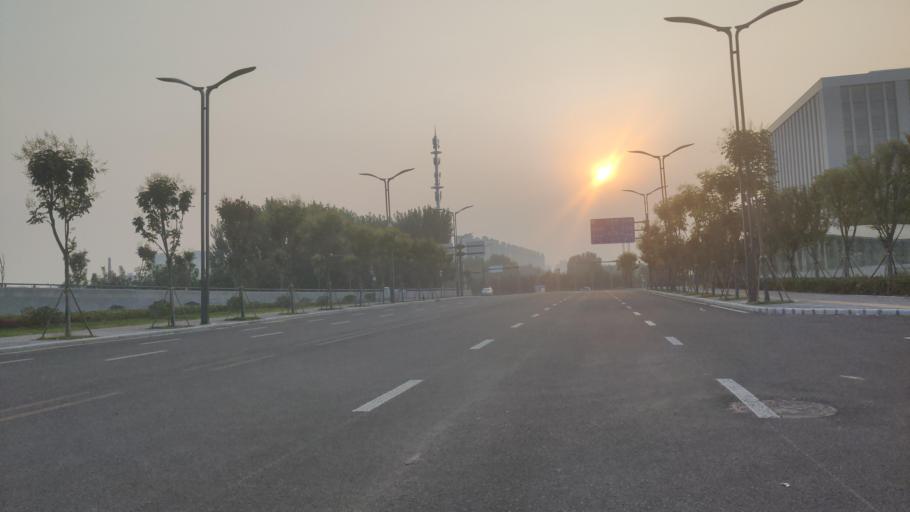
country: CN
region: Henan Sheng
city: Zhongyuanlu
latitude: 35.7629
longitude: 115.1432
